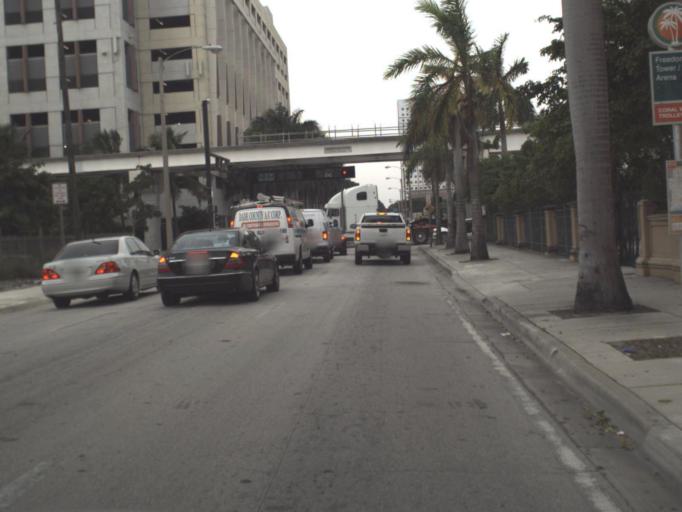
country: US
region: Florida
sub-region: Miami-Dade County
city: Miami
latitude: 25.7801
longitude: -80.1898
